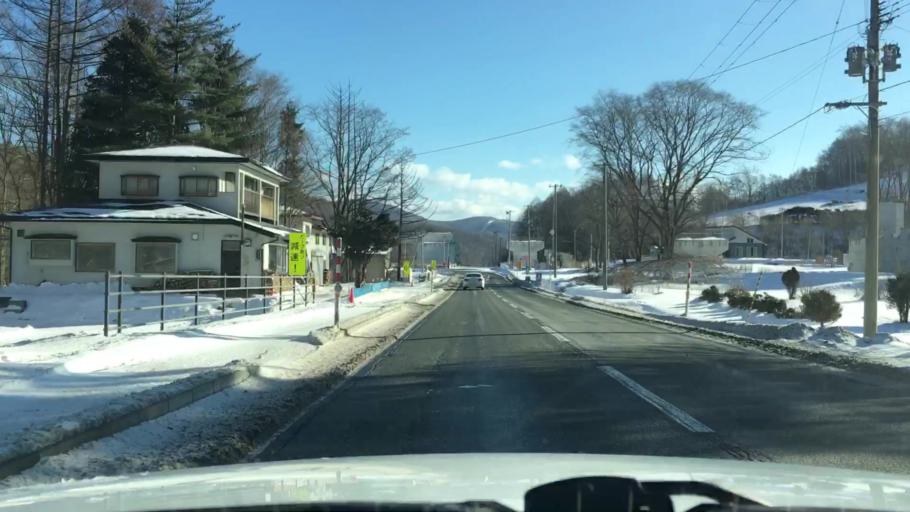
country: JP
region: Iwate
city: Morioka-shi
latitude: 39.6427
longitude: 141.3799
